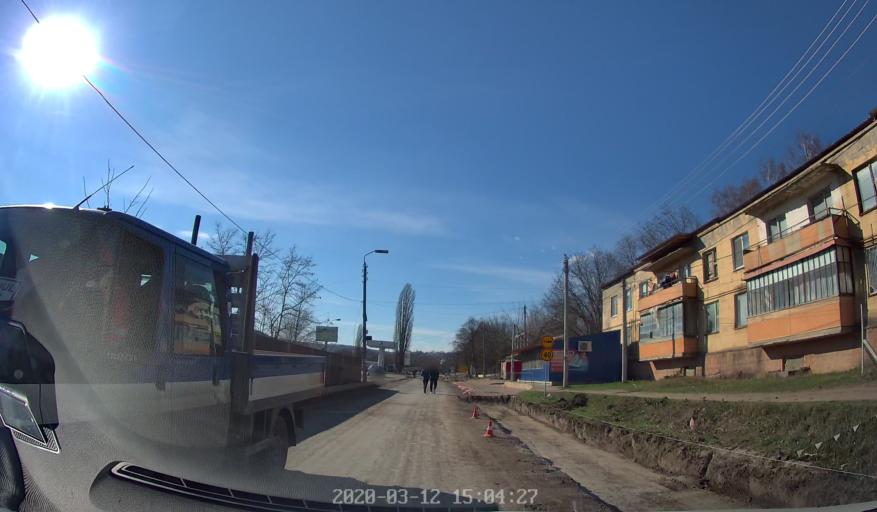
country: MD
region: Telenesti
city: Cocieri
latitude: 47.2212
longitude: 29.0184
